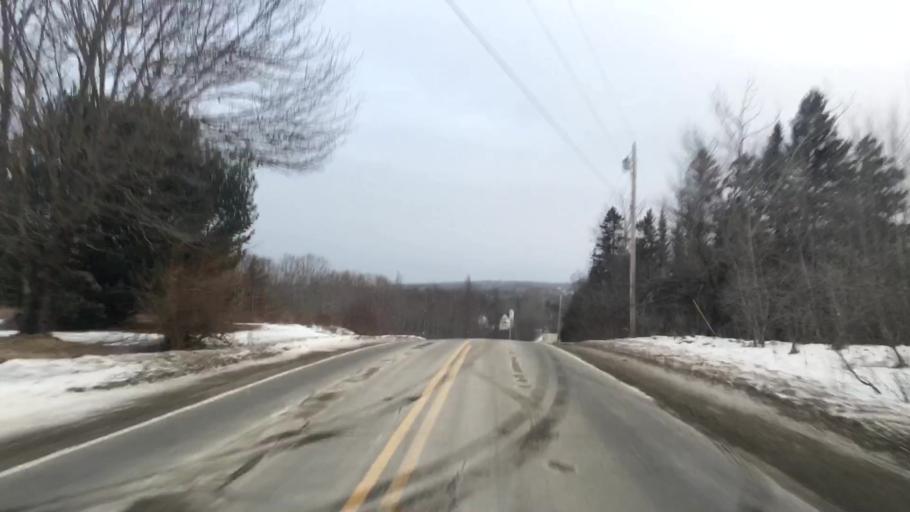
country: US
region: Maine
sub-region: Hancock County
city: Franklin
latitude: 44.6833
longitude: -68.3514
